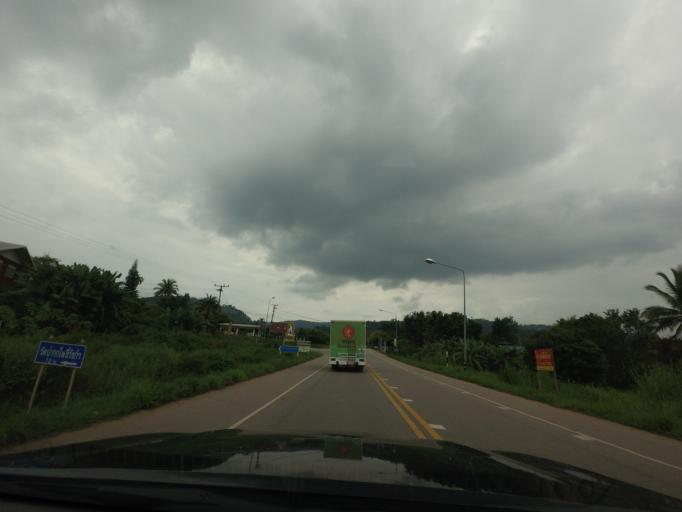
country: TH
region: Loei
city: Dan Sai
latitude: 17.2900
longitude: 101.2442
